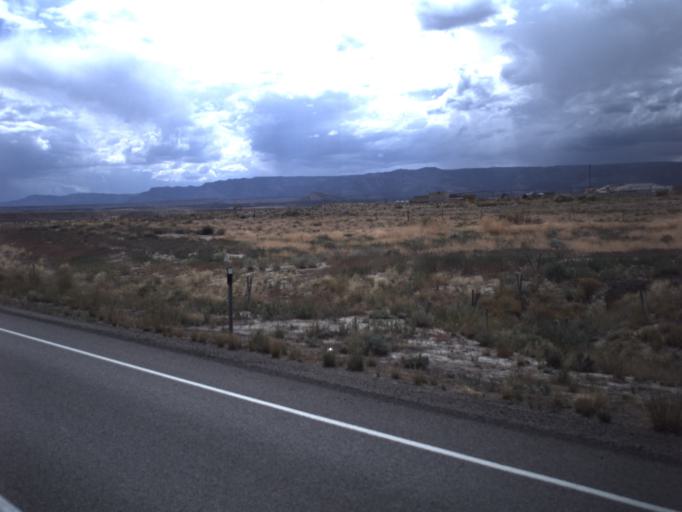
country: US
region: Utah
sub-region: Carbon County
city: Price
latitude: 39.5339
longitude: -110.8169
